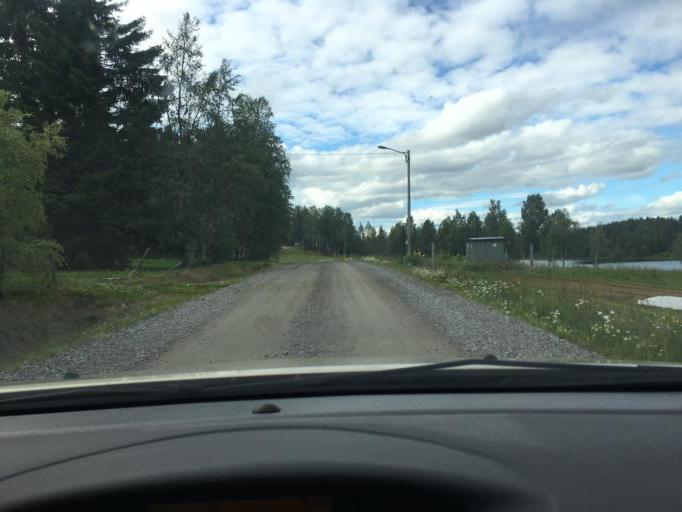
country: SE
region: Norrbotten
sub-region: Overkalix Kommun
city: OEverkalix
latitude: 66.0873
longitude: 22.8884
